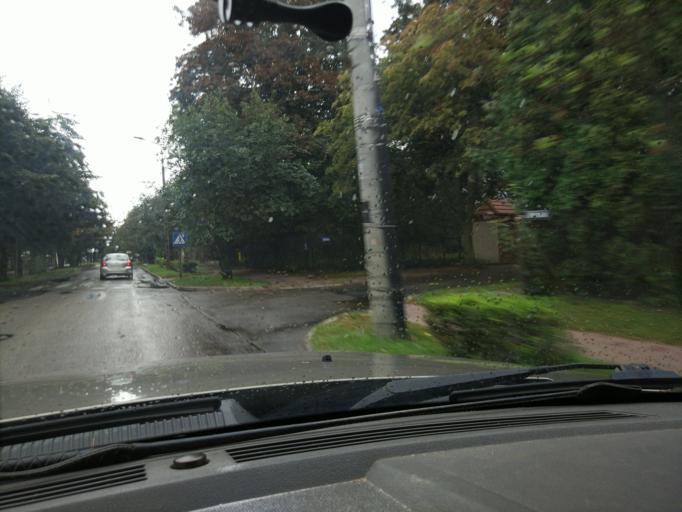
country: PL
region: Masovian Voivodeship
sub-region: Powiat grodziski
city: Podkowa Lesna
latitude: 52.1249
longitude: 20.7227
